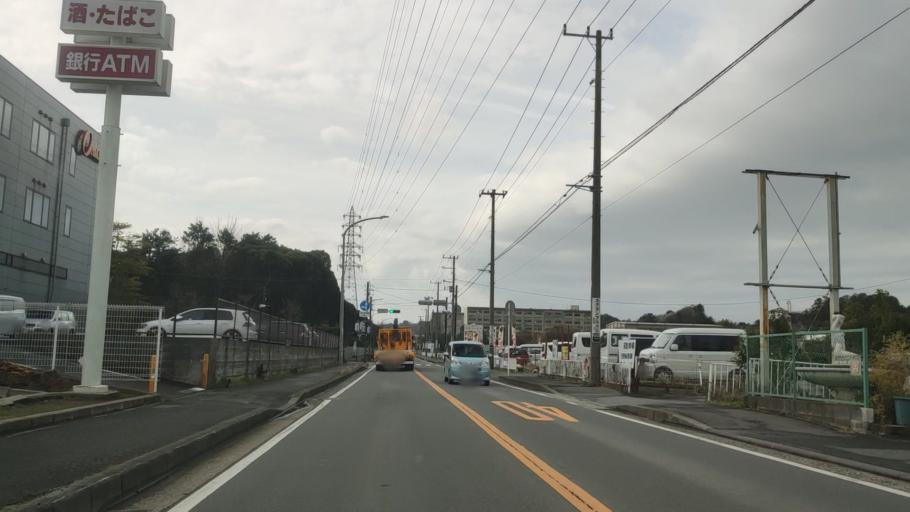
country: JP
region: Kanagawa
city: Fujisawa
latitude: 35.3773
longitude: 139.5255
